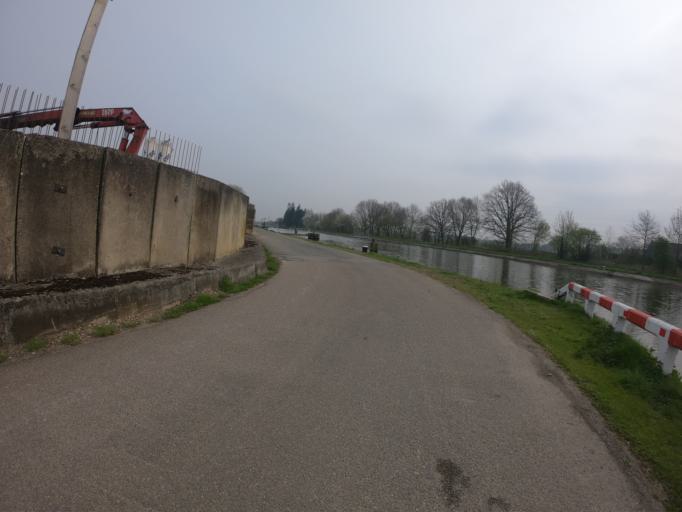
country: BE
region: Flanders
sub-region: Provincie Limburg
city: Lanaken
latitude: 50.8995
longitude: 5.6792
